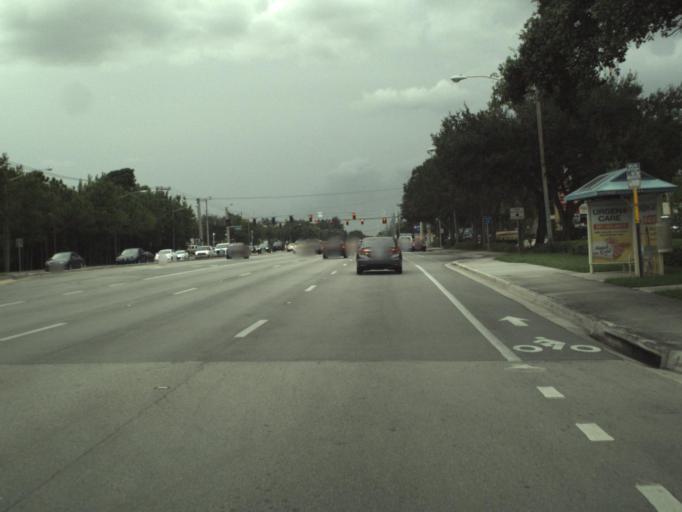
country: US
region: Florida
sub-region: Palm Beach County
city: Boca Pointe
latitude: 26.3680
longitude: -80.1845
